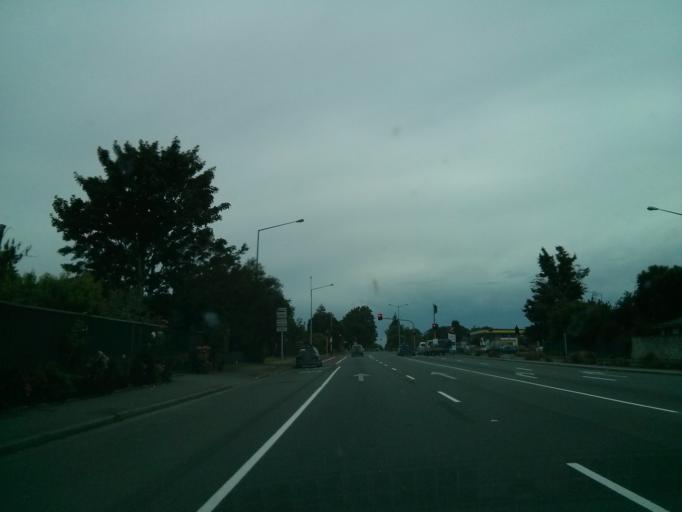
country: NZ
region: Canterbury
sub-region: Waimakariri District
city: Kaiapoi
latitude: -43.4502
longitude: 172.6291
